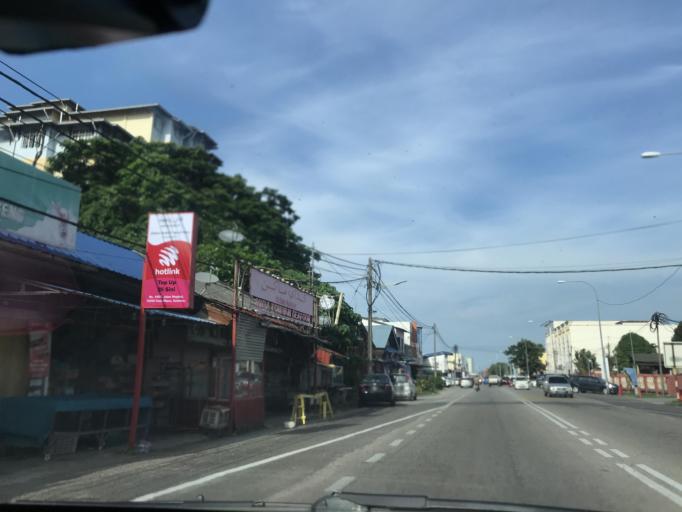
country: MY
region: Kelantan
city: Kota Bharu
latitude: 6.1248
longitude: 102.2475
